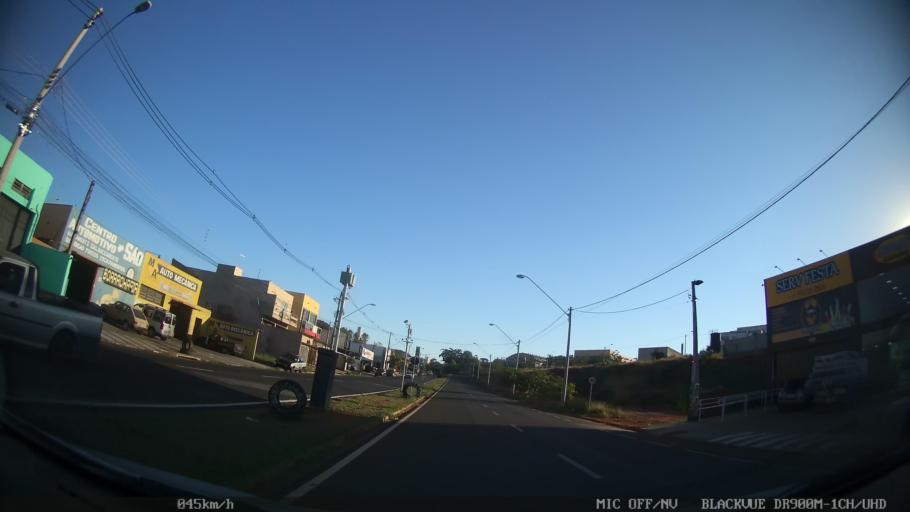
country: BR
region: Sao Paulo
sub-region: Sao Jose Do Rio Preto
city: Sao Jose do Rio Preto
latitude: -20.7921
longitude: -49.3517
